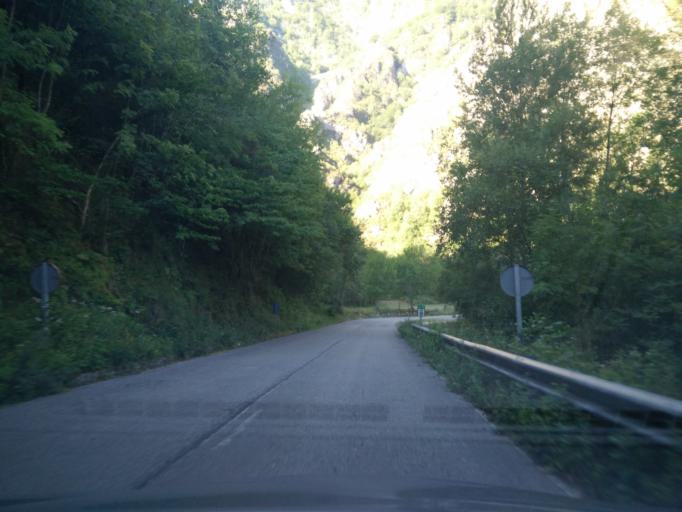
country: ES
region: Asturias
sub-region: Province of Asturias
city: Amieva
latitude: 43.2171
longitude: -5.2051
